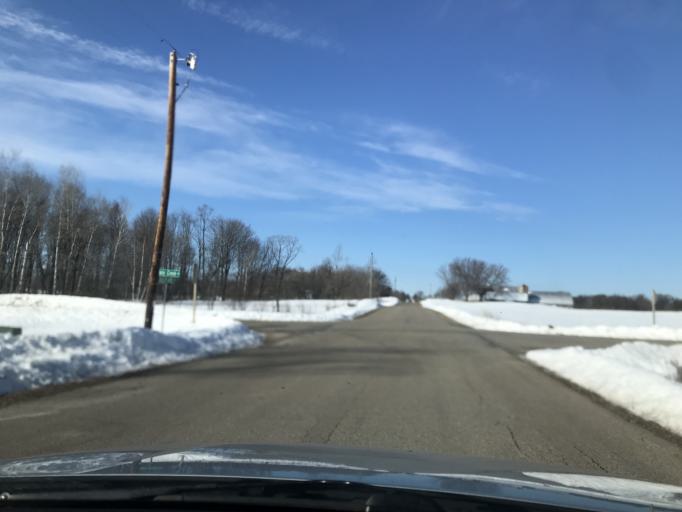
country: US
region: Wisconsin
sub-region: Oconto County
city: Gillett
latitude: 44.9396
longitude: -88.2446
